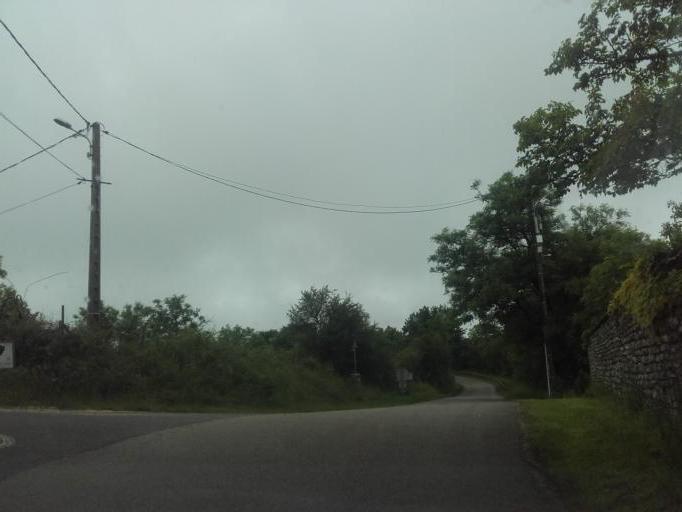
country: FR
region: Bourgogne
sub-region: Departement de la Cote-d'Or
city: Nolay
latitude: 46.9919
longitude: 4.6936
